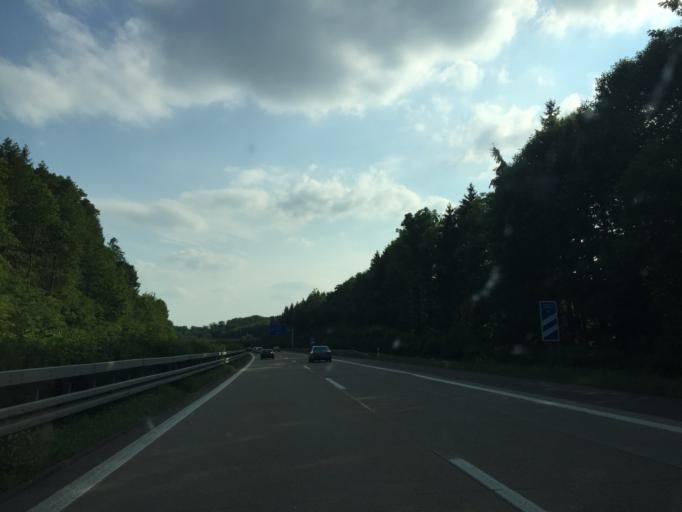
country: DE
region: Baden-Wuerttemberg
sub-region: Regierungsbezirk Stuttgart
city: Mockmuhl
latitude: 49.2849
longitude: 9.3600
